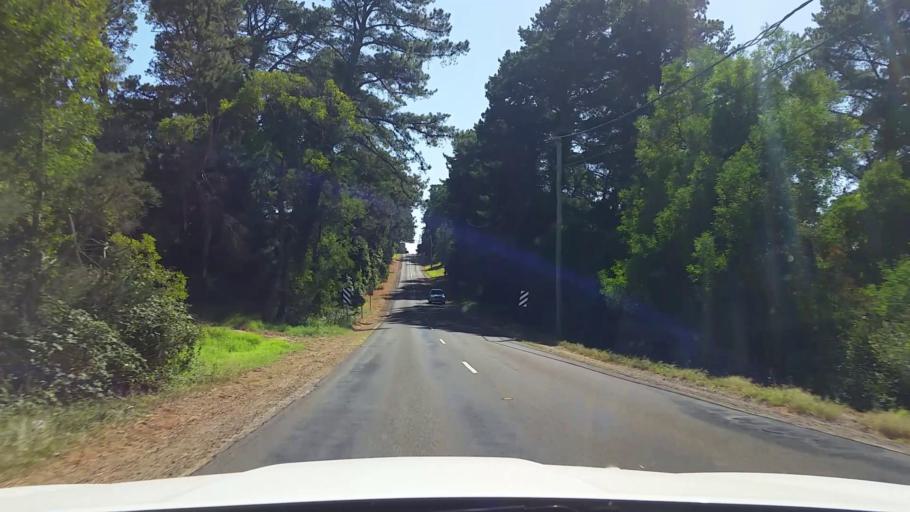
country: AU
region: Victoria
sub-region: Mornington Peninsula
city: Hastings
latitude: -38.3083
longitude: 145.1457
